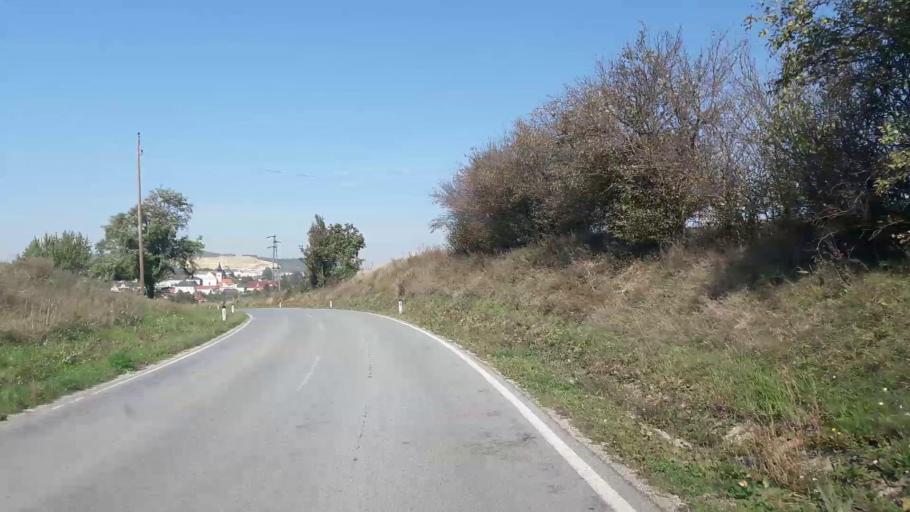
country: AT
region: Lower Austria
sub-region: Politischer Bezirk Korneuburg
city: Ernstbrunn
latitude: 48.5190
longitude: 16.3620
